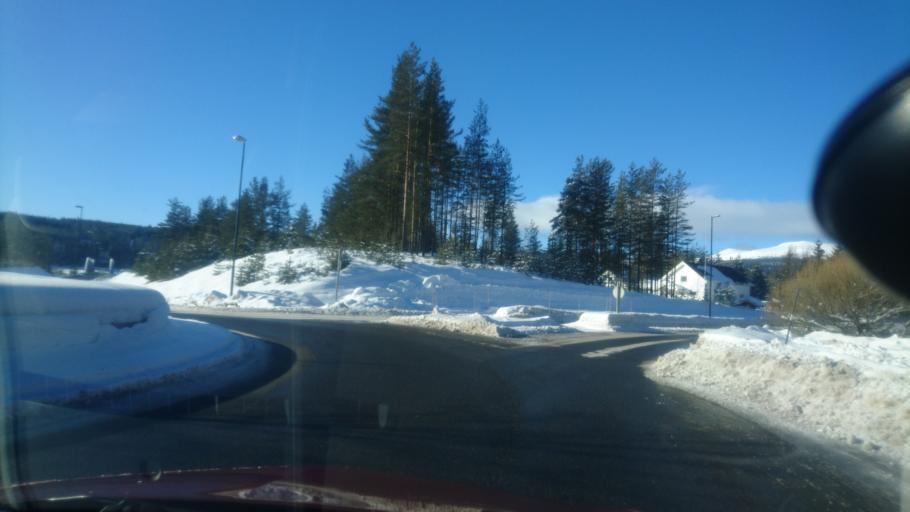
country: NO
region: Hedmark
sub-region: Trysil
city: Innbygda
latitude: 61.2744
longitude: 12.3072
